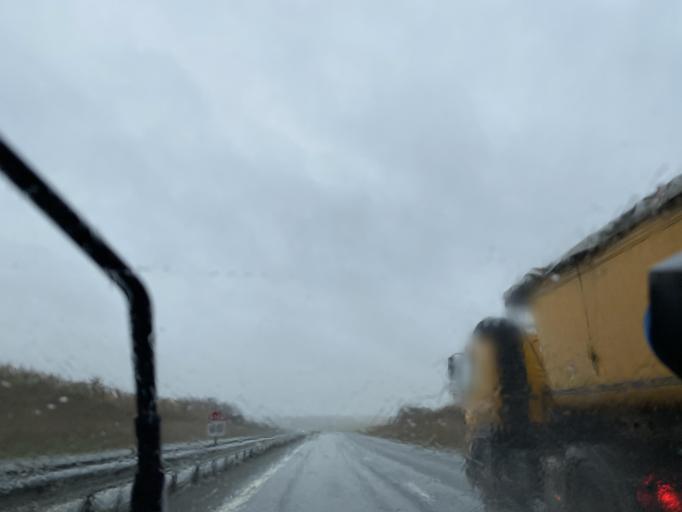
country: FR
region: Centre
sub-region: Departement d'Eure-et-Loir
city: Leves
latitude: 48.5298
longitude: 1.4558
